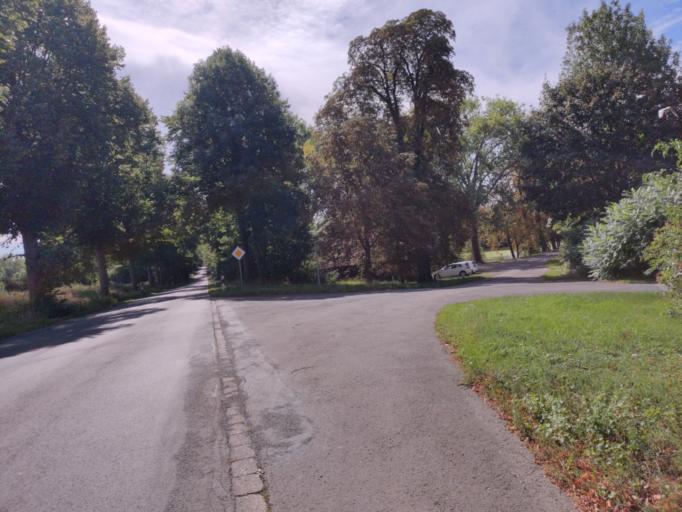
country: DE
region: Lower Saxony
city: Sehlde
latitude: 52.0498
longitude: 10.2836
